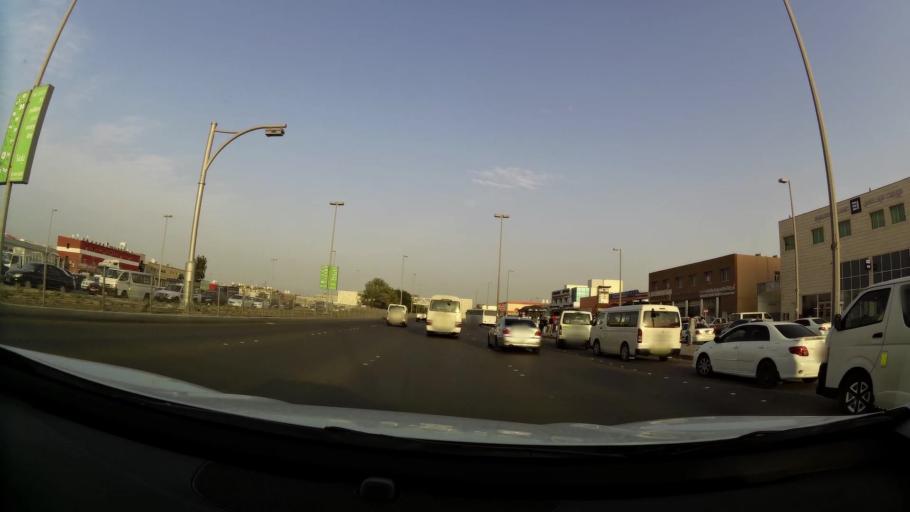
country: AE
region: Abu Dhabi
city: Abu Dhabi
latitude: 24.3732
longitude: 54.5133
